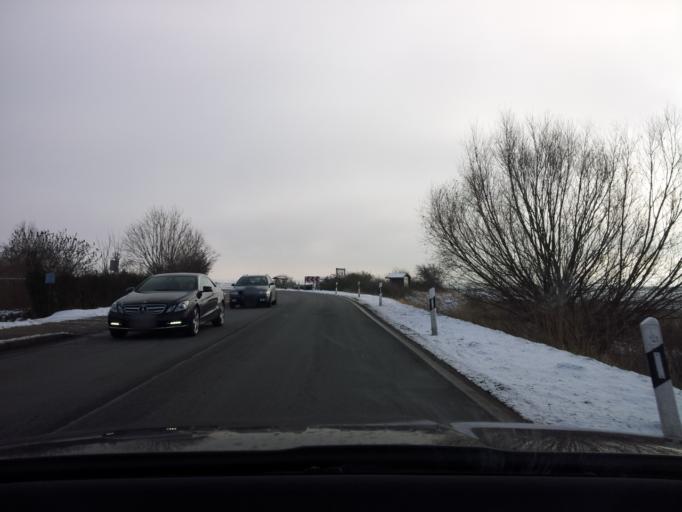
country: DE
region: Mecklenburg-Vorpommern
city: Blowatz
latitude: 53.9737
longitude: 11.4651
